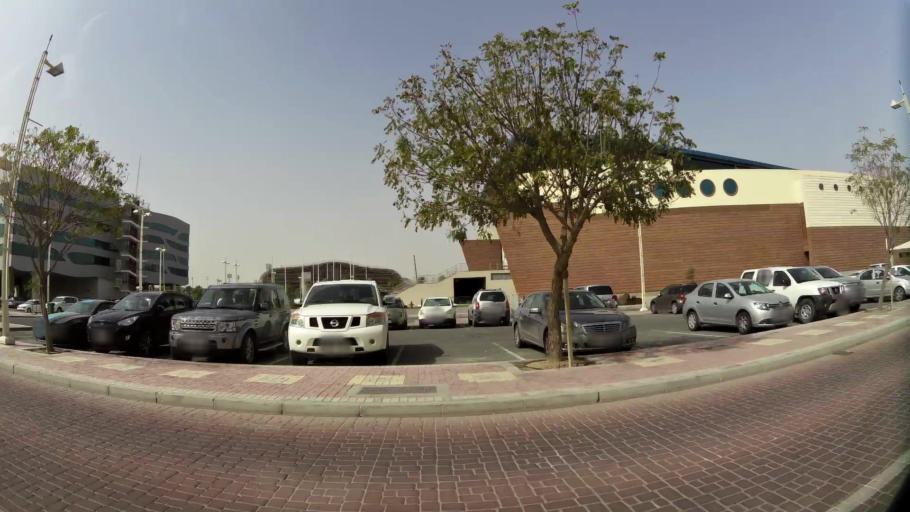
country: QA
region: Baladiyat ar Rayyan
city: Ar Rayyan
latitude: 25.2631
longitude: 51.4424
